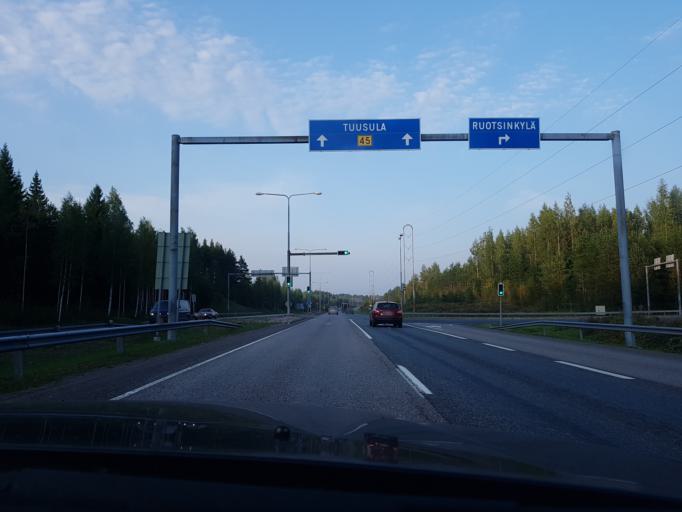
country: FI
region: Uusimaa
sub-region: Helsinki
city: Tuusula
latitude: 60.3651
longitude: 25.0070
